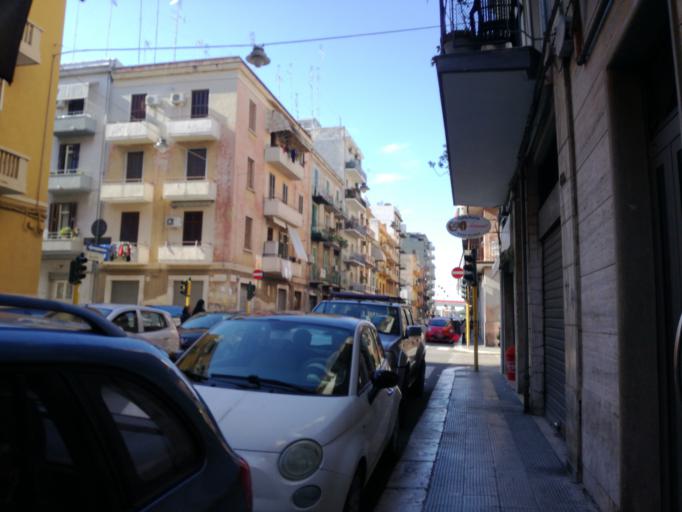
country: IT
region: Apulia
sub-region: Provincia di Bari
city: Bari
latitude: 41.1211
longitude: 16.8544
